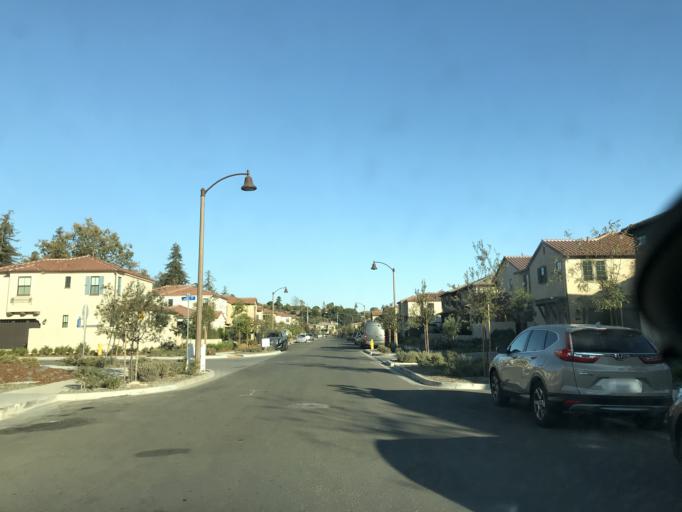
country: US
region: California
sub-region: Santa Barbara County
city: Goleta
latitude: 34.4490
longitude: -119.8133
